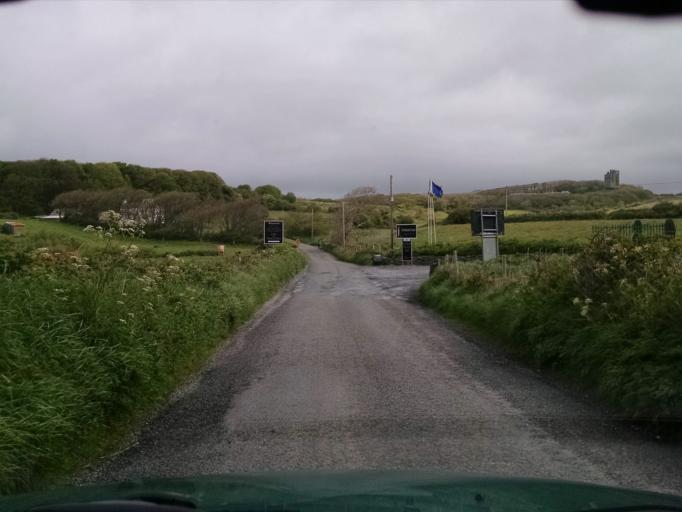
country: IE
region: Connaught
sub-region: County Galway
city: Bearna
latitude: 53.0419
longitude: -9.3463
